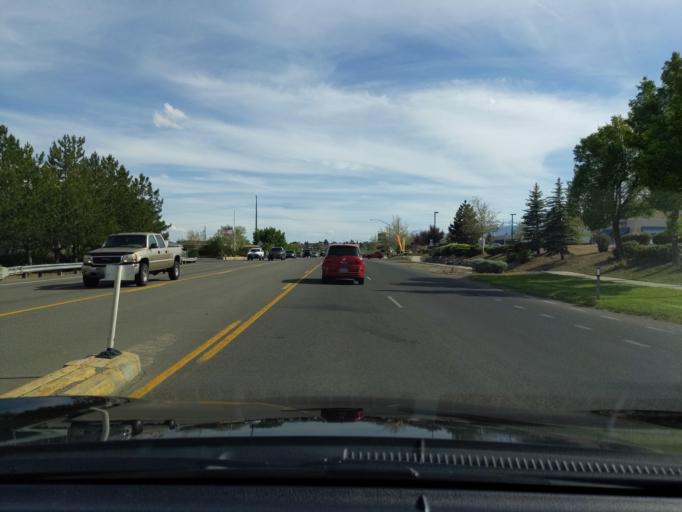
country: US
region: Nevada
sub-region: Washoe County
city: Sun Valley
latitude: 39.5777
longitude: -119.7805
